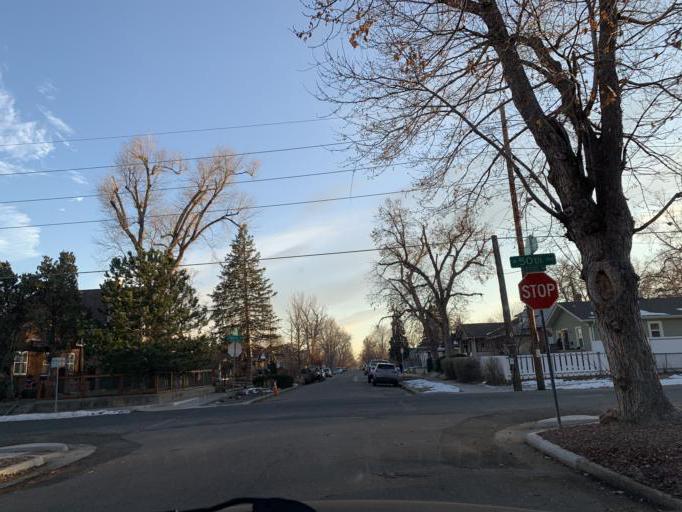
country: US
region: Colorado
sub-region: Adams County
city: Berkley
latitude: 39.7876
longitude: -105.0381
